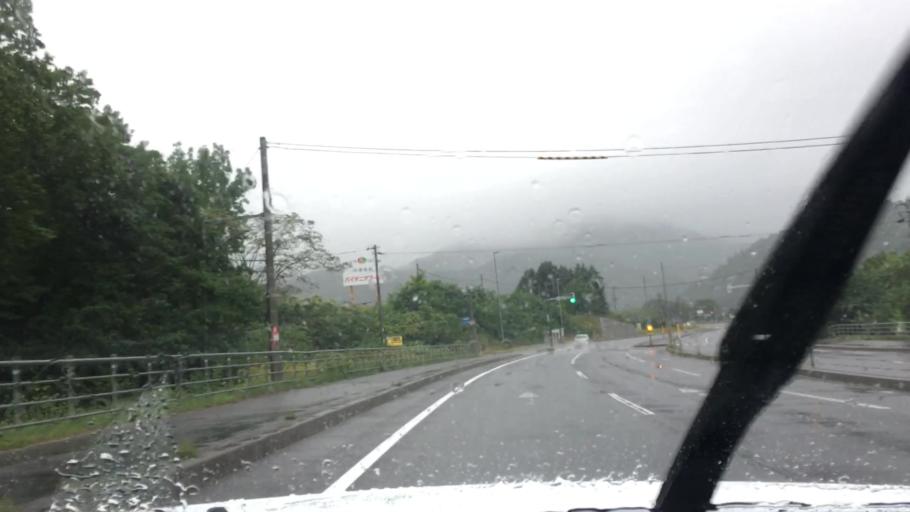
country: JP
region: Hokkaido
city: Sapporo
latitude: 42.9615
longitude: 141.2230
